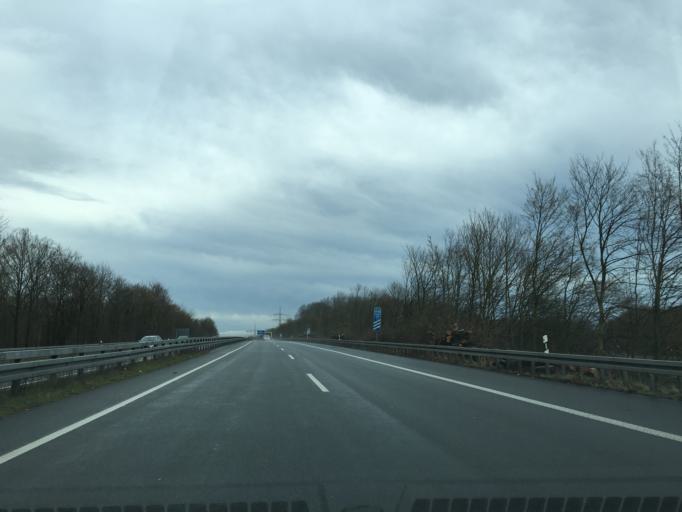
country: DE
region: North Rhine-Westphalia
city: Marl
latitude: 51.6474
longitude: 7.0394
